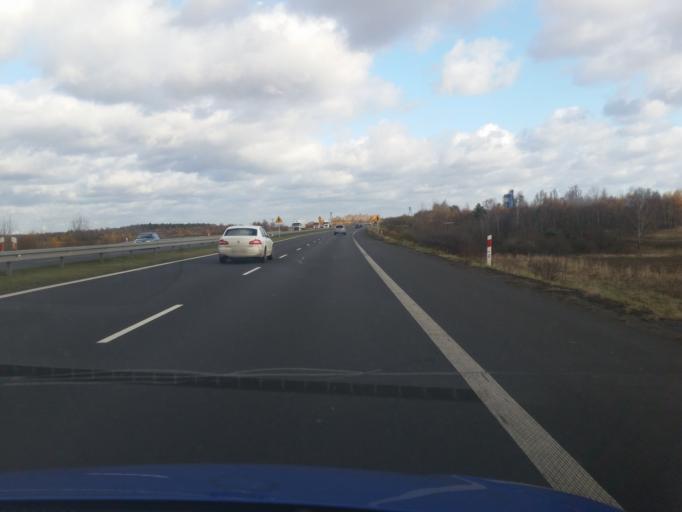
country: PL
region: Silesian Voivodeship
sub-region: Powiat czestochowski
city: Koscielec
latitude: 50.8835
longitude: 19.1689
